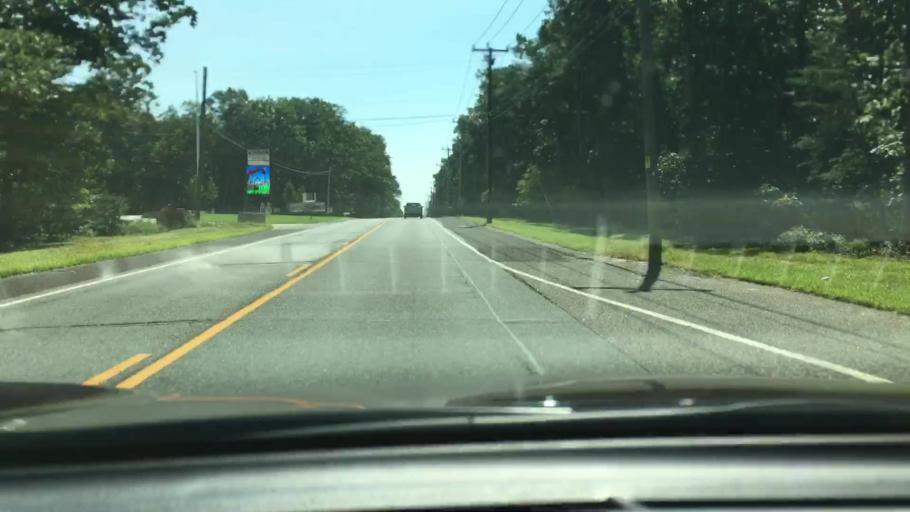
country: US
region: New Jersey
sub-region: Cumberland County
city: Millville
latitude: 39.3816
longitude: -74.9730
